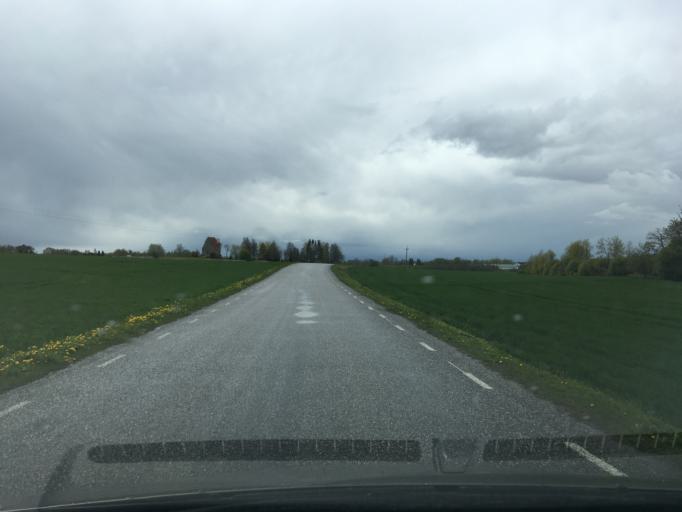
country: EE
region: Harju
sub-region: Joelaehtme vald
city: Loo
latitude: 59.4239
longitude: 24.9873
